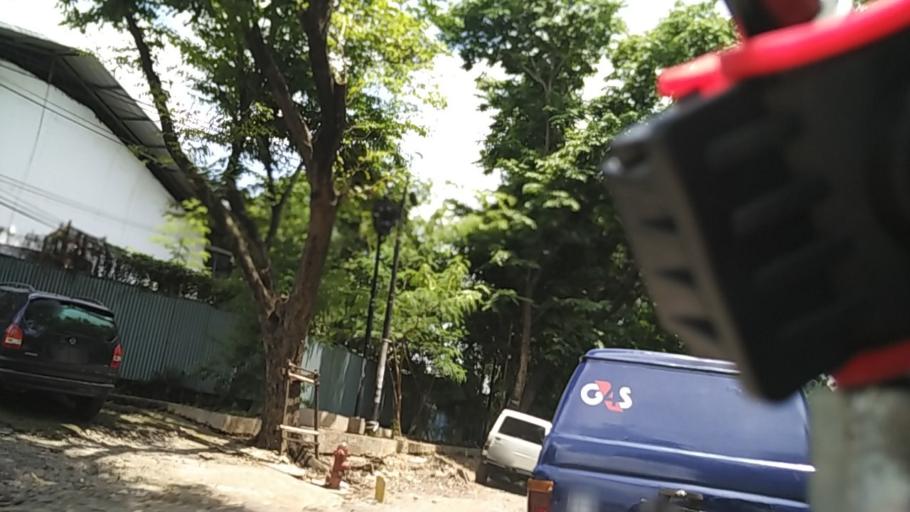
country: ID
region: Central Java
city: Semarang
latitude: -7.0030
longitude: 110.3926
